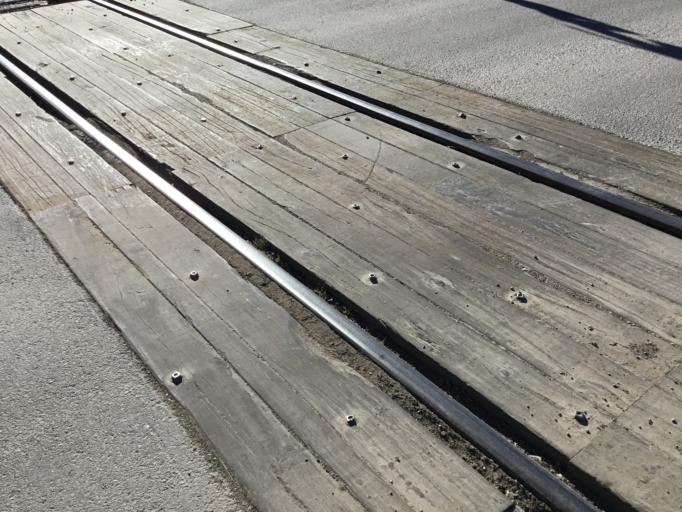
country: US
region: Kansas
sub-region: McPherson County
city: McPherson
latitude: 38.3705
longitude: -97.6723
